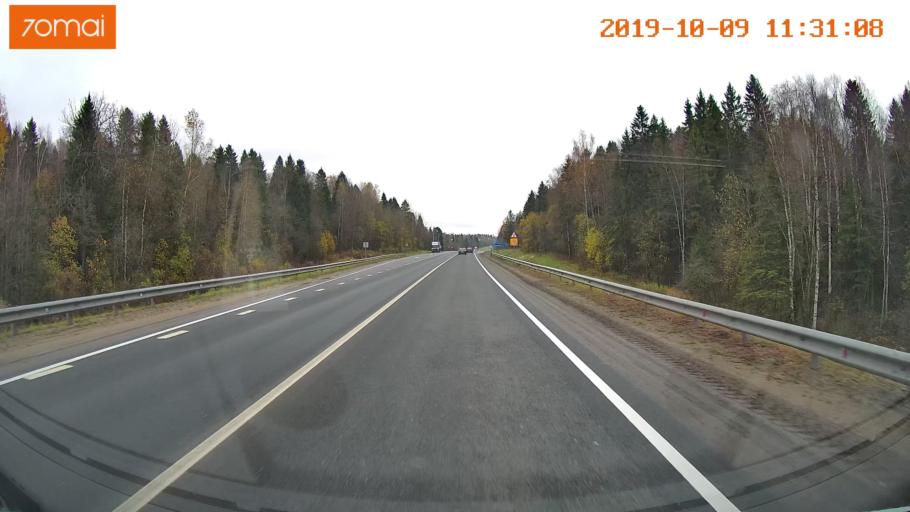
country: RU
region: Vologda
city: Gryazovets
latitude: 59.0480
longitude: 40.0900
